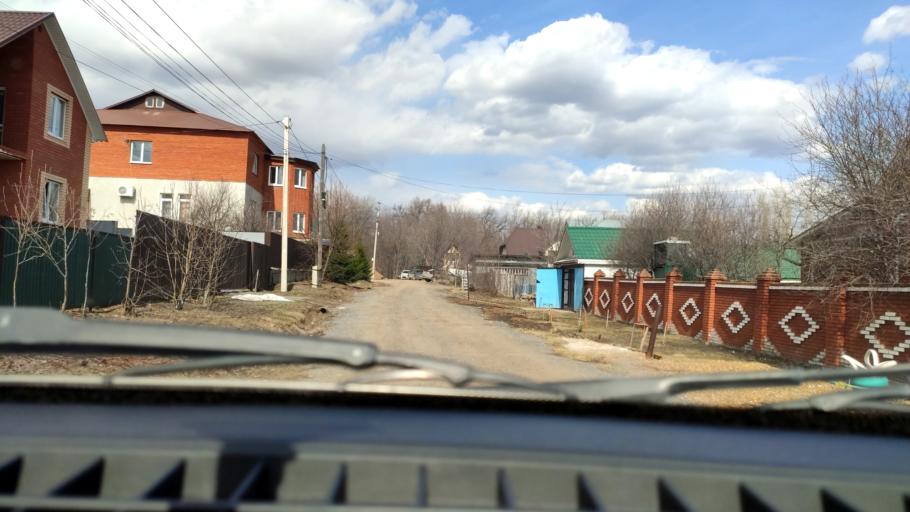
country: RU
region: Bashkortostan
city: Mikhaylovka
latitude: 54.8213
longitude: 55.8956
